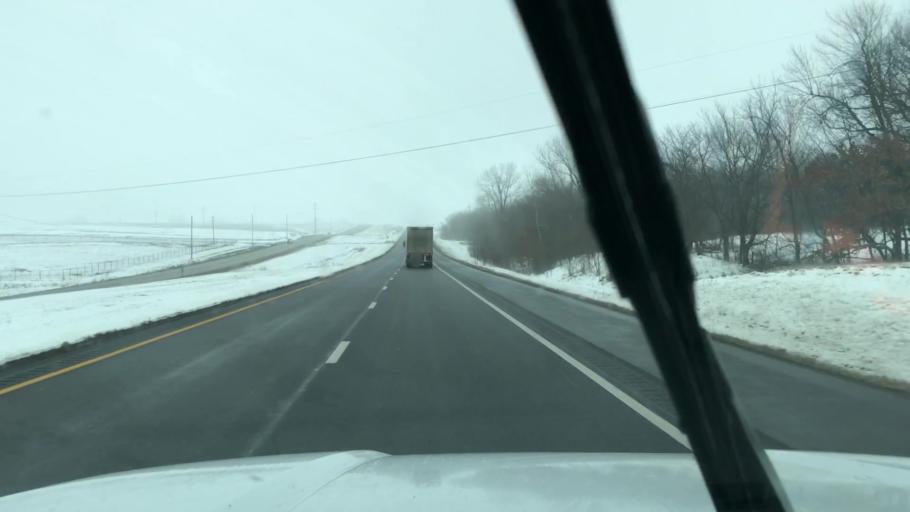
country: US
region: Missouri
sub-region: DeKalb County
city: Maysville
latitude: 39.7620
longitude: -94.4585
